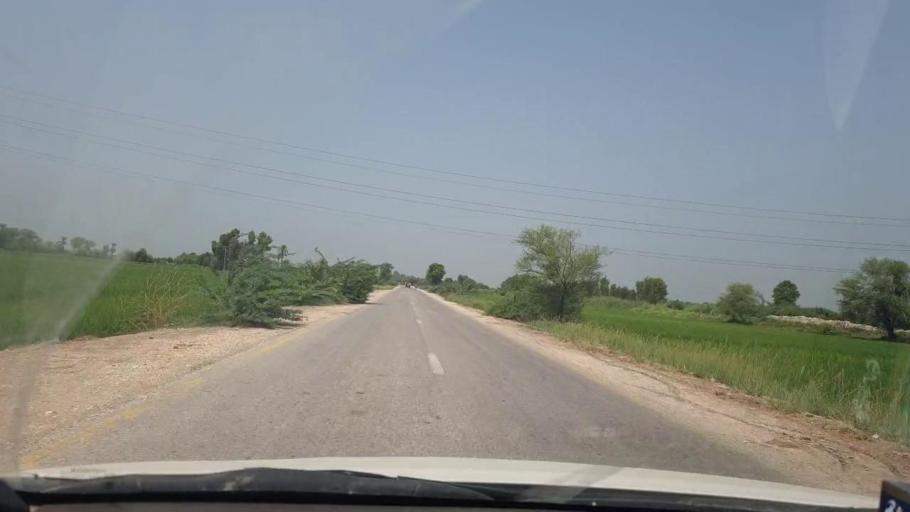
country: PK
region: Sindh
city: Shikarpur
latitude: 27.9540
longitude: 68.6765
